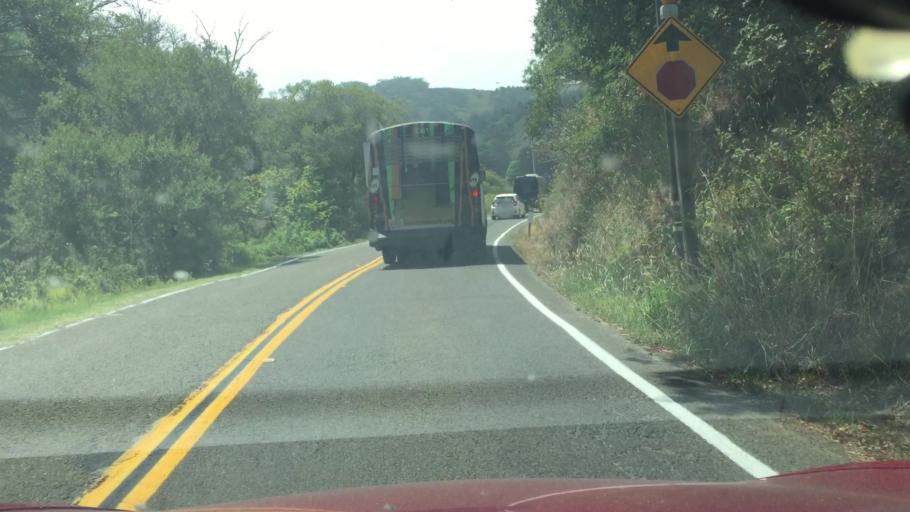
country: US
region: California
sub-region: Marin County
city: Tamalpais Valley
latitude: 37.8771
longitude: -122.5819
